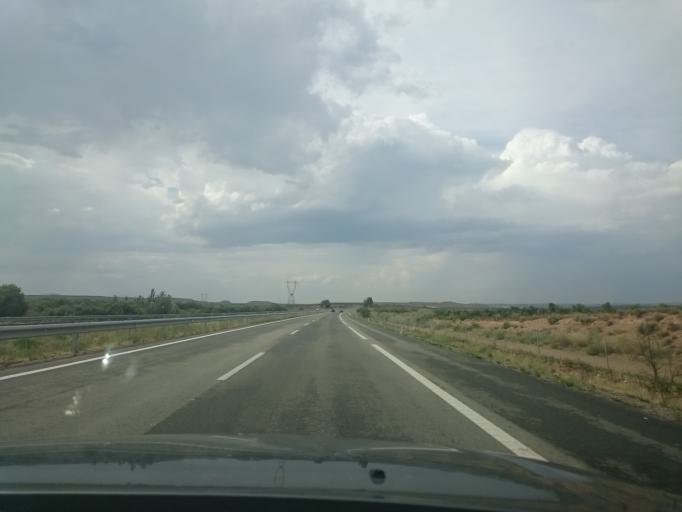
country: ES
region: La Rioja
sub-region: Provincia de La Rioja
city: Rincon de Soto
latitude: 42.1724
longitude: -1.8333
